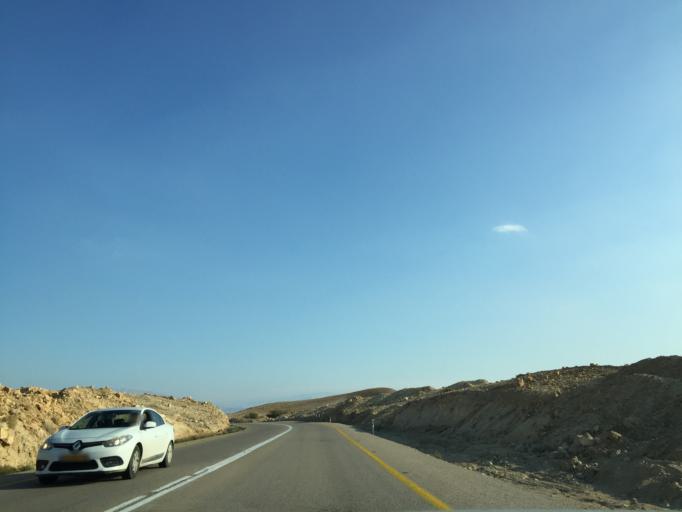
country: IL
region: Southern District
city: `En Boqeq
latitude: 31.1639
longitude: 35.3224
